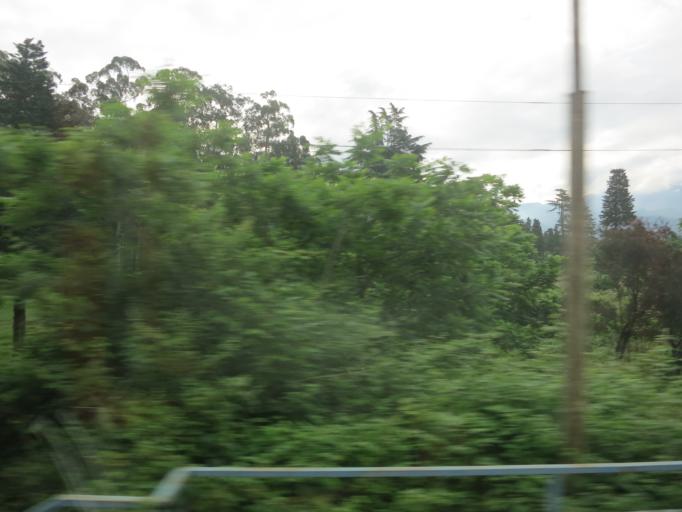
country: GE
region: Ajaria
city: Makhinjauri
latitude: 41.7210
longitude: 41.7290
